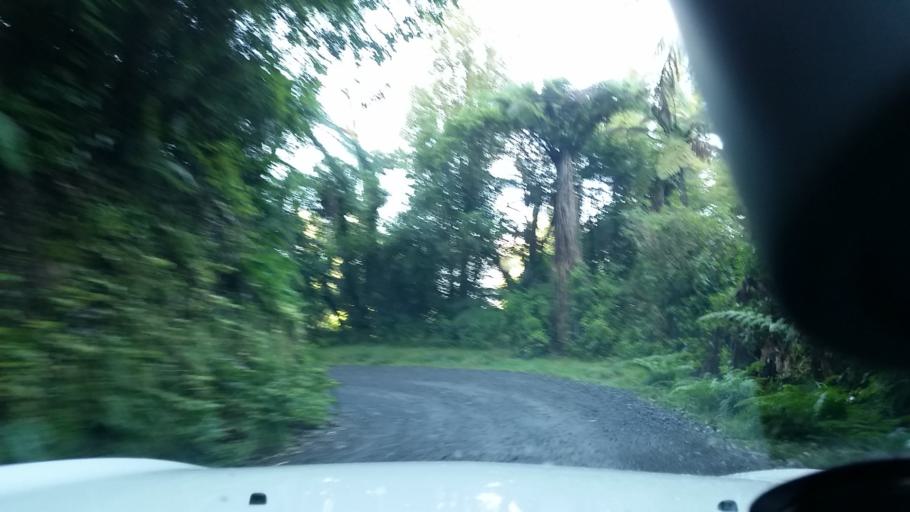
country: NZ
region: Bay of Plenty
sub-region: Kawerau District
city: Kawerau
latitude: -38.0191
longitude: 176.5933
